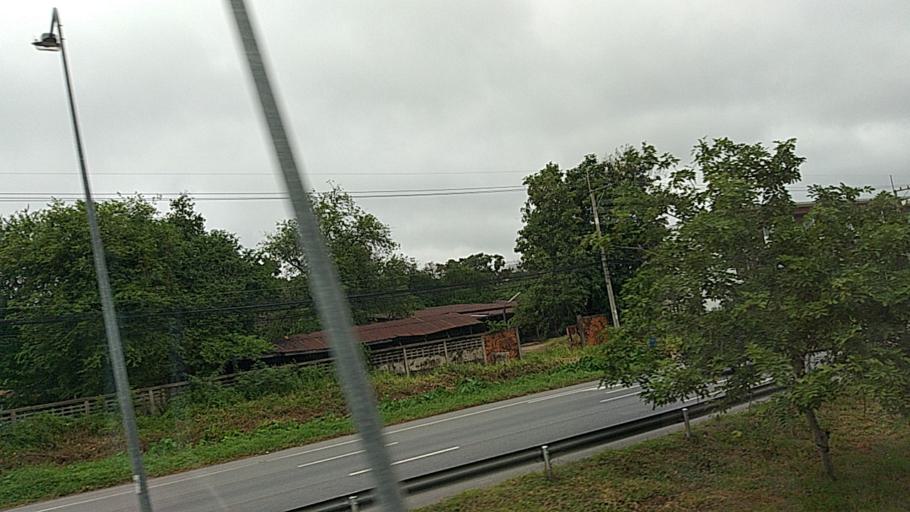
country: TH
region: Nakhon Ratchasima
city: Nakhon Ratchasima
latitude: 15.0345
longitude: 102.1437
